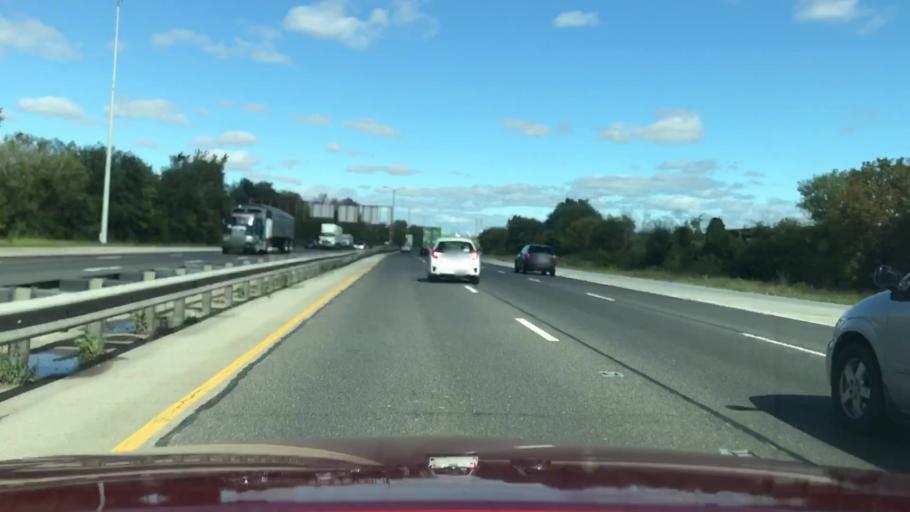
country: US
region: Illinois
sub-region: Cook County
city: Burnham
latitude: 41.6247
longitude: -87.5789
